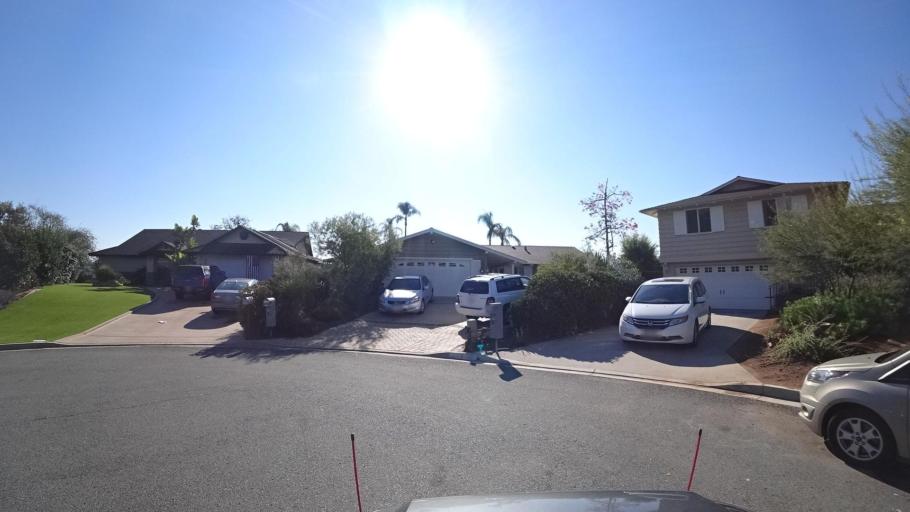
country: US
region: California
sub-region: San Diego County
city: Casa de Oro-Mount Helix
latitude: 32.7617
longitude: -116.9867
